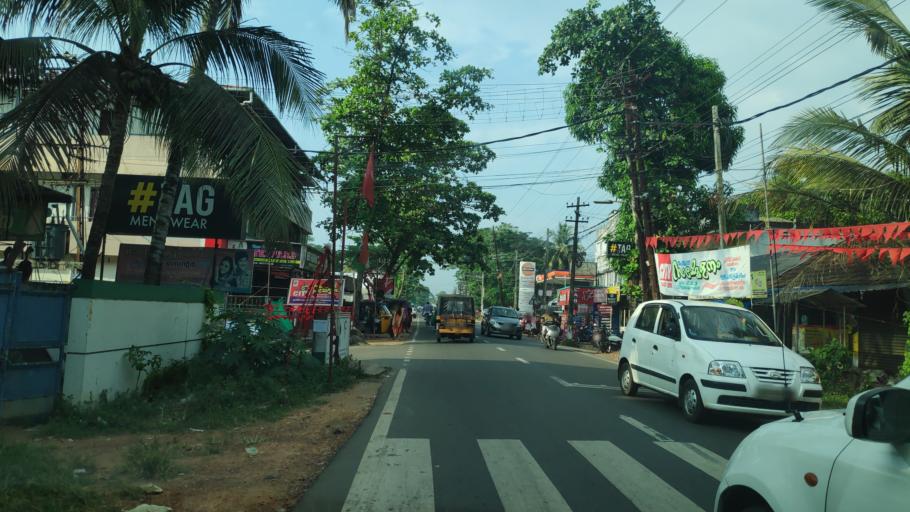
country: IN
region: Kerala
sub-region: Alappuzha
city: Alleppey
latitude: 9.5099
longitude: 76.3391
